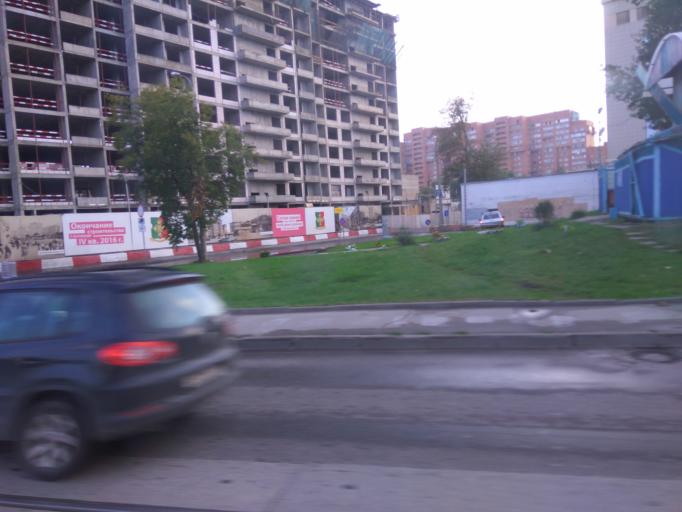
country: RU
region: Moskovskaya
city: Bogorodskoye
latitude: 55.8018
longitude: 37.7105
